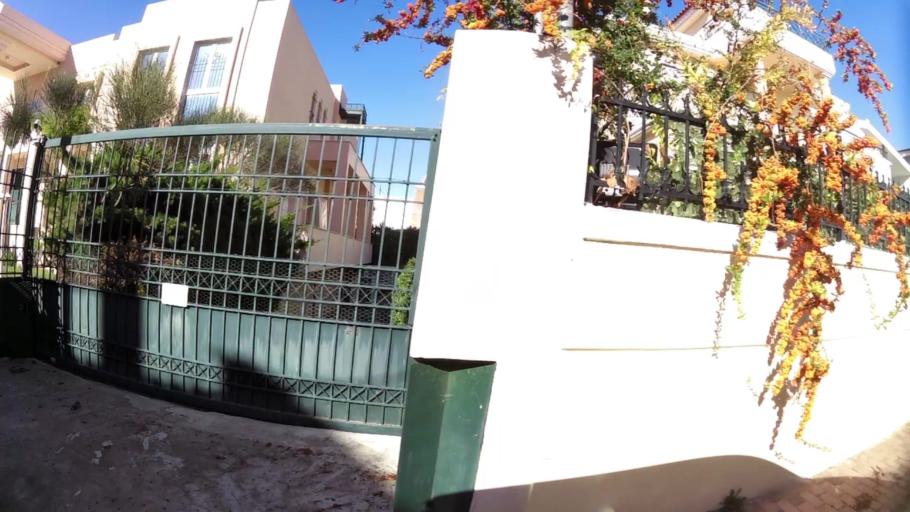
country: GR
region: Attica
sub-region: Nomarchia Athinas
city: Nea Erythraia
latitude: 38.0975
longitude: 23.8166
